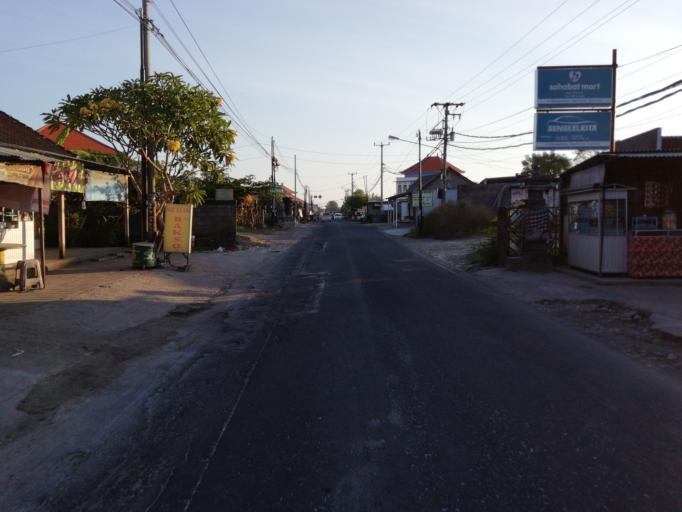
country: ID
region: Bali
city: Jimbaran
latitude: -8.8269
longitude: 115.1820
